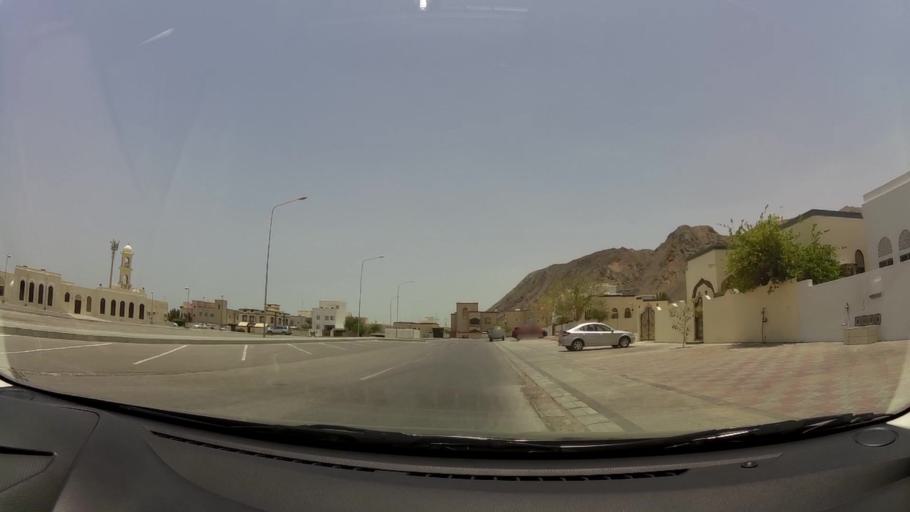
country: OM
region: Muhafazat Masqat
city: Bawshar
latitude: 23.5658
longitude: 58.4241
